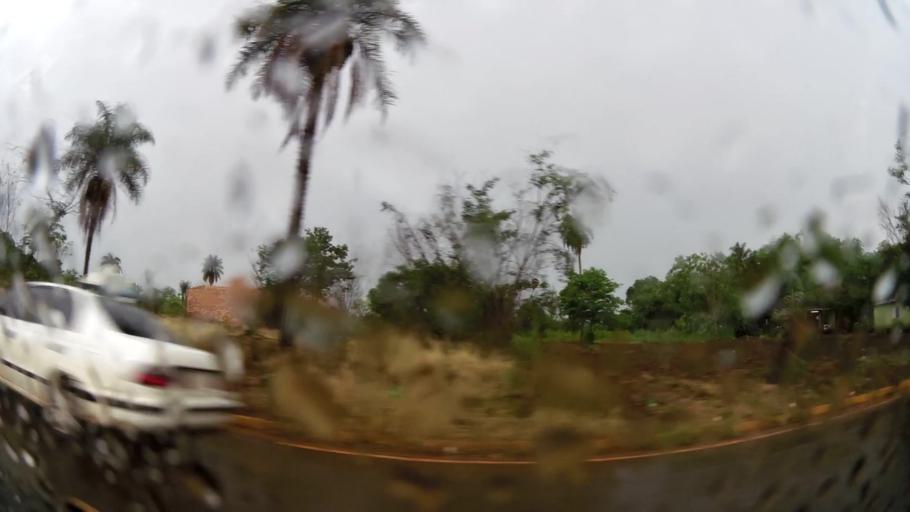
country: PY
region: Alto Parana
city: Presidente Franco
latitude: -25.5430
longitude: -54.6784
